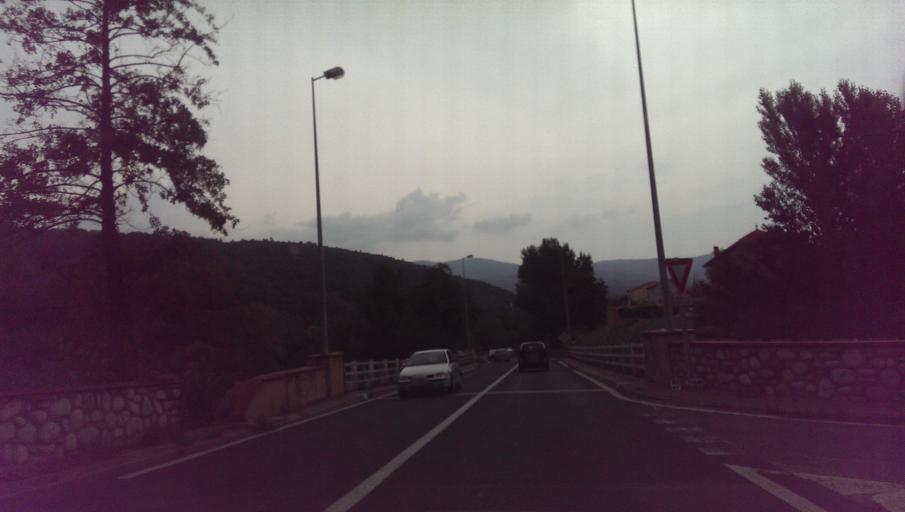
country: FR
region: Languedoc-Roussillon
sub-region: Departement des Pyrenees-Orientales
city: Ria-Sirach
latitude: 42.6143
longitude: 2.4115
